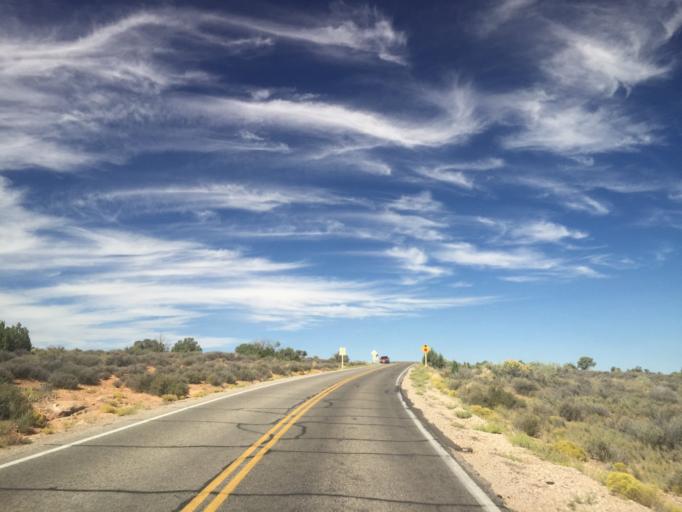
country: US
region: Utah
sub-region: Grand County
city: Moab
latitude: 38.7031
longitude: -109.5612
